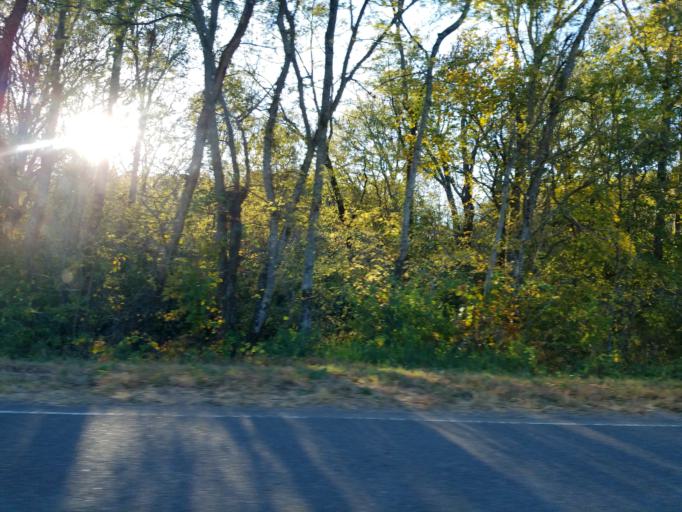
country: US
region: Georgia
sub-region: Bartow County
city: Euharlee
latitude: 34.2558
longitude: -84.9602
